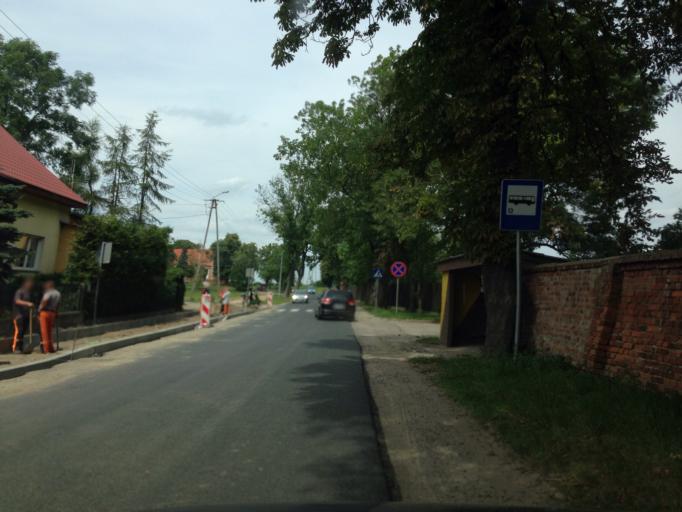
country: PL
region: Kujawsko-Pomorskie
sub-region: Powiat brodnicki
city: Brodnica
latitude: 53.3009
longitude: 19.3981
